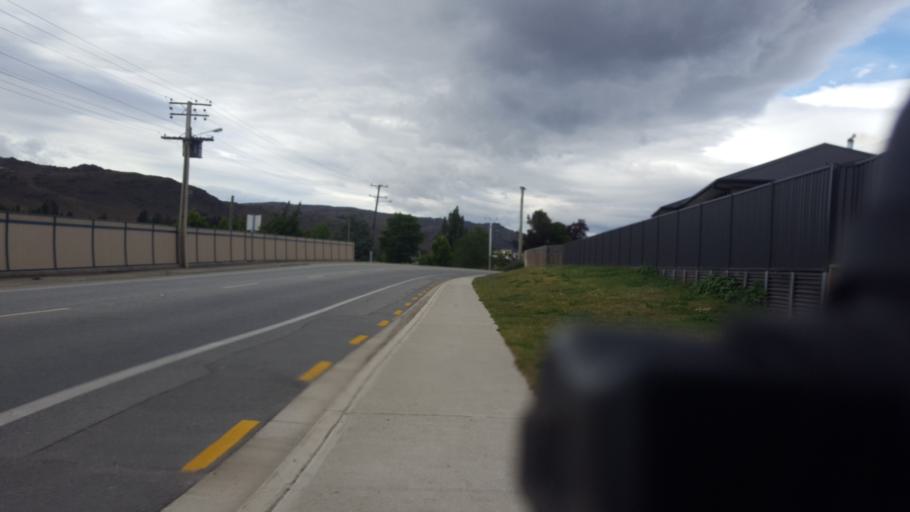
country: NZ
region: Otago
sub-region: Queenstown-Lakes District
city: Wanaka
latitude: -45.2460
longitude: 169.4022
